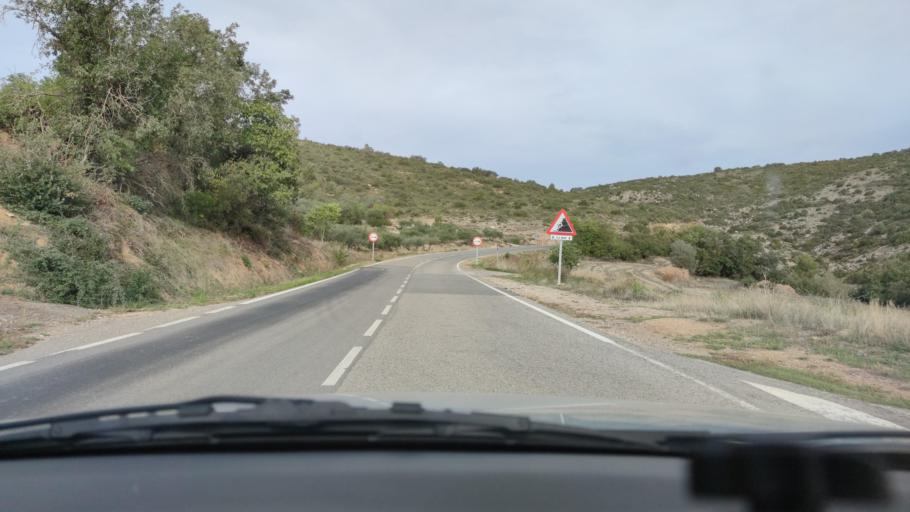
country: ES
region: Catalonia
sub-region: Provincia de Lleida
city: Artesa de Segre
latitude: 41.9293
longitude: 1.0559
